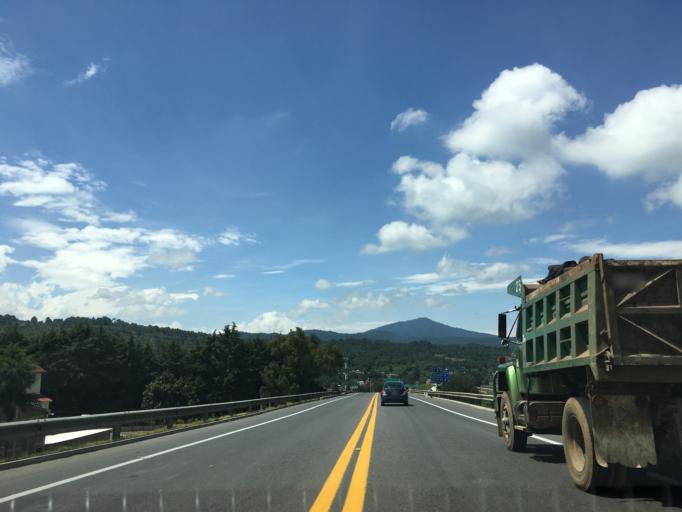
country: MX
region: Michoacan
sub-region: Patzcuaro
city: Colonia Vista Bella (Lomas del Peaje)
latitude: 19.4953
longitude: -101.5949
